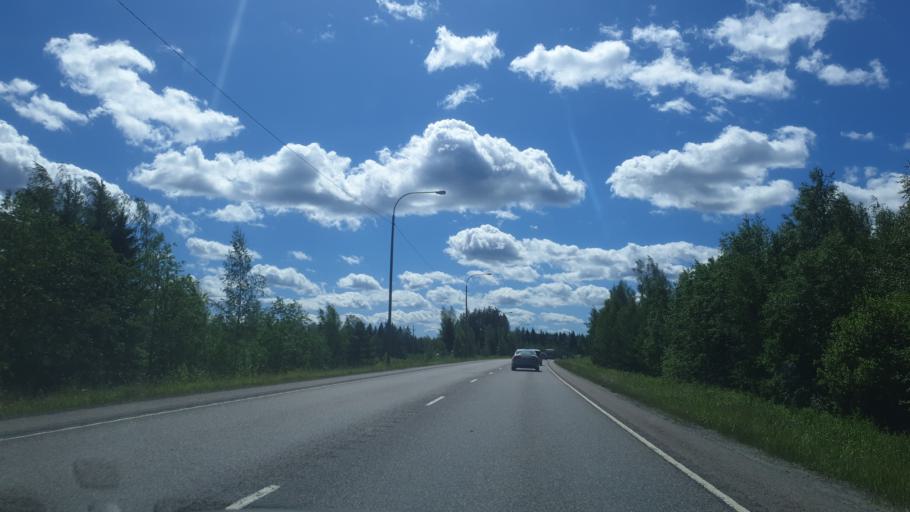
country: FI
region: Northern Savo
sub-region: Varkaus
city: Leppaevirta
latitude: 62.4047
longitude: 27.8257
